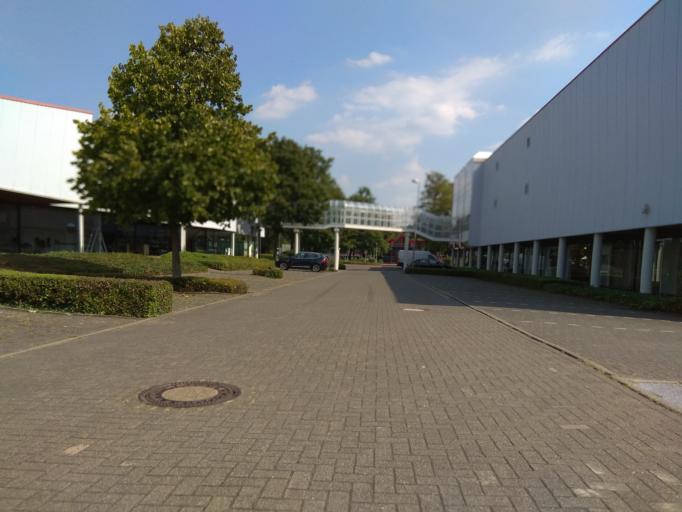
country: DE
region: North Rhine-Westphalia
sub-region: Regierungsbezirk Munster
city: Klein Reken
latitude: 51.7234
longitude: 7.0347
